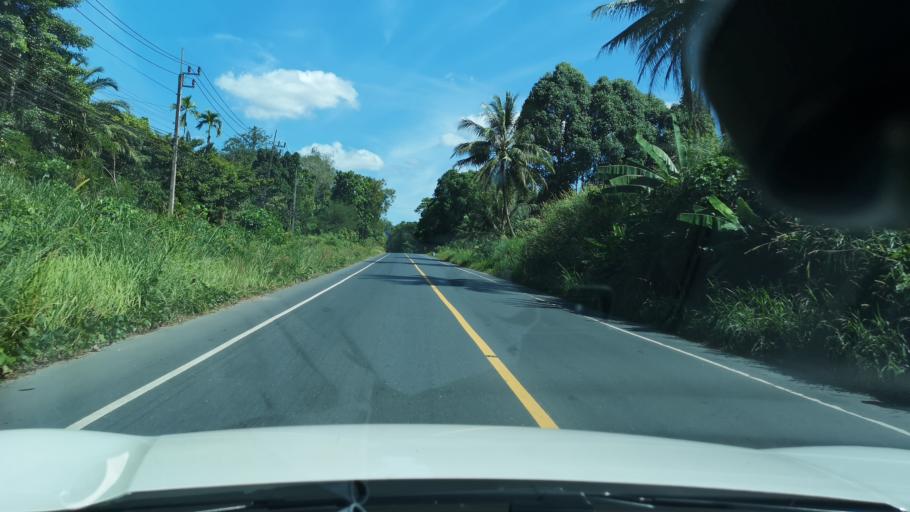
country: TH
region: Phangnga
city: Phang Nga
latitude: 8.5337
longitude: 98.5046
